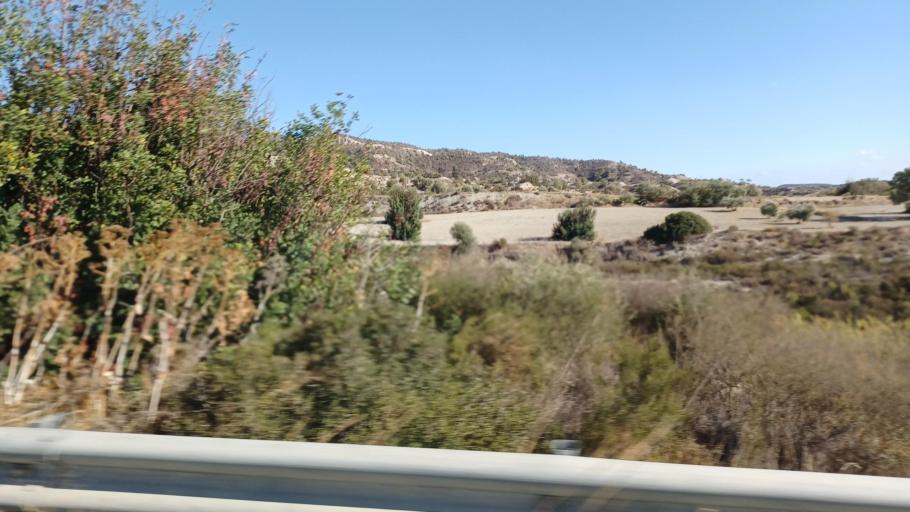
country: CY
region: Limassol
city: Pyrgos
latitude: 34.7591
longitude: 33.2281
